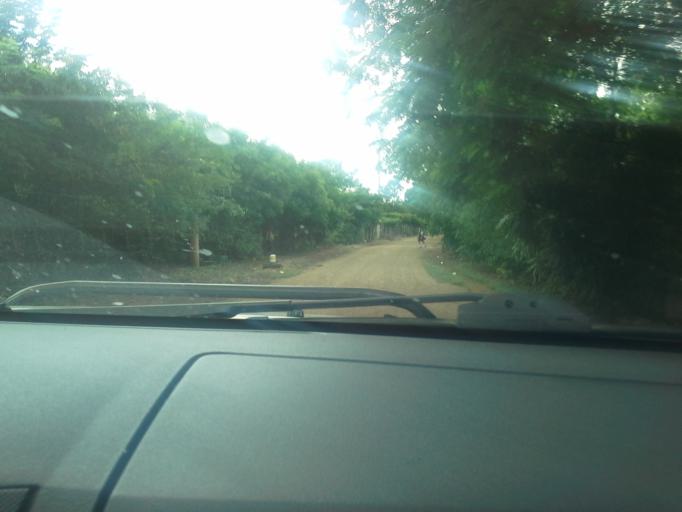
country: NI
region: Matagalpa
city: Ciudad Dario
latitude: 12.8132
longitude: -86.1913
